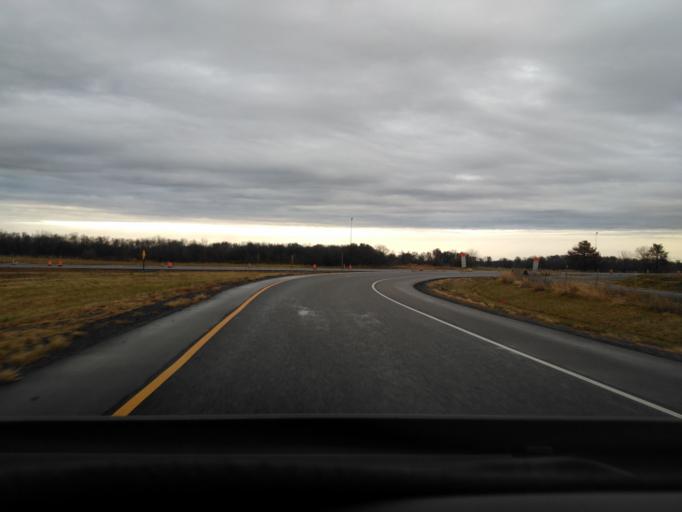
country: US
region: Illinois
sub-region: Bond County
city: Greenville
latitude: 38.8713
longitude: -89.3817
